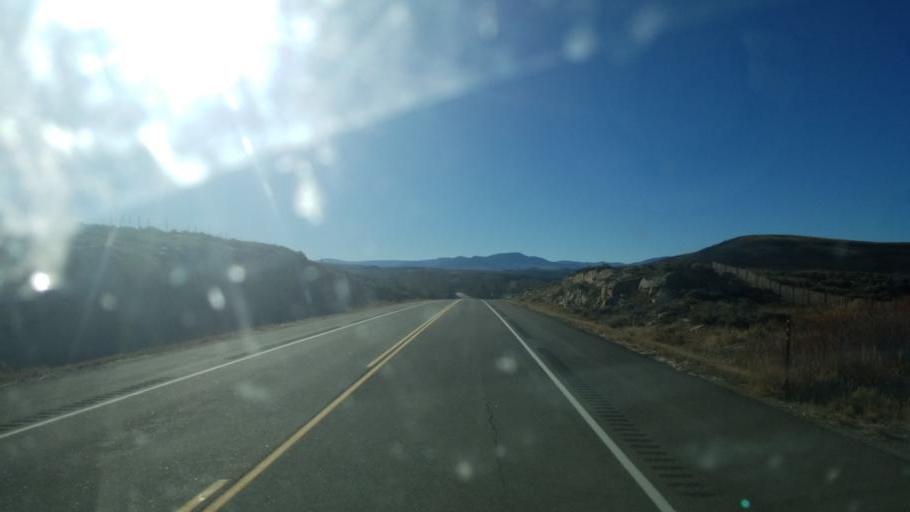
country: US
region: Colorado
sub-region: Gunnison County
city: Gunnison
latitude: 38.5079
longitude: -106.7328
